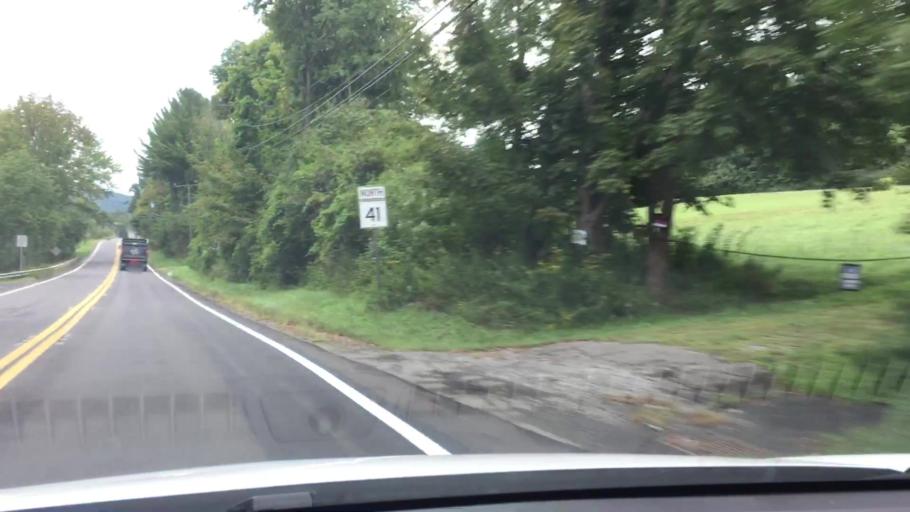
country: US
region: Massachusetts
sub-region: Berkshire County
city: Richmond
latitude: 42.3688
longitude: -73.3680
